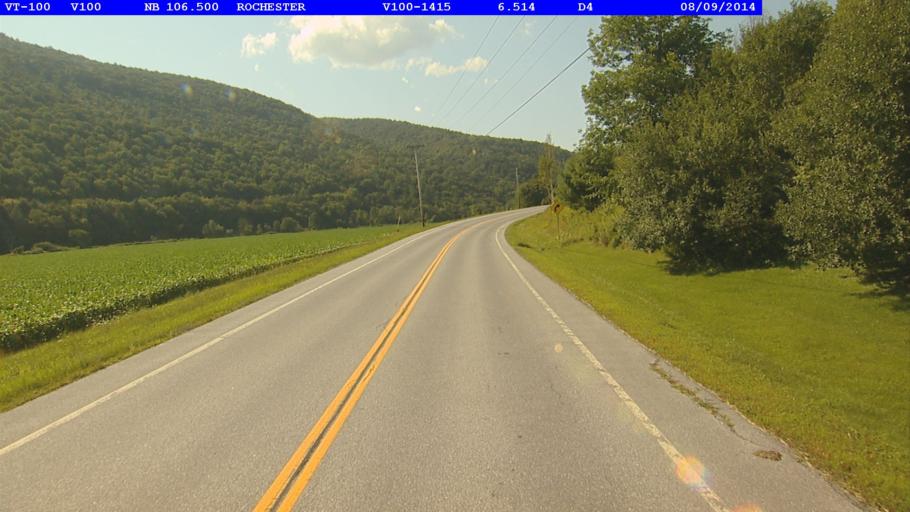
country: US
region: Vermont
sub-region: Orange County
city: Randolph
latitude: 43.8893
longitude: -72.8166
